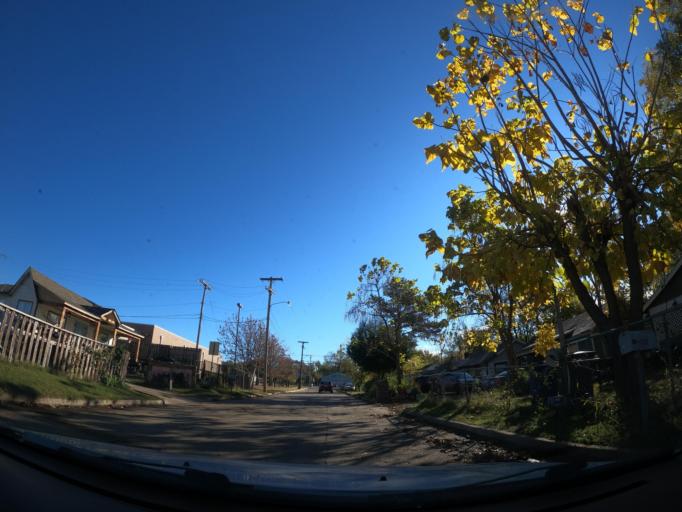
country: US
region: Oklahoma
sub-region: Tulsa County
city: Tulsa
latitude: 36.1762
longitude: -95.9595
